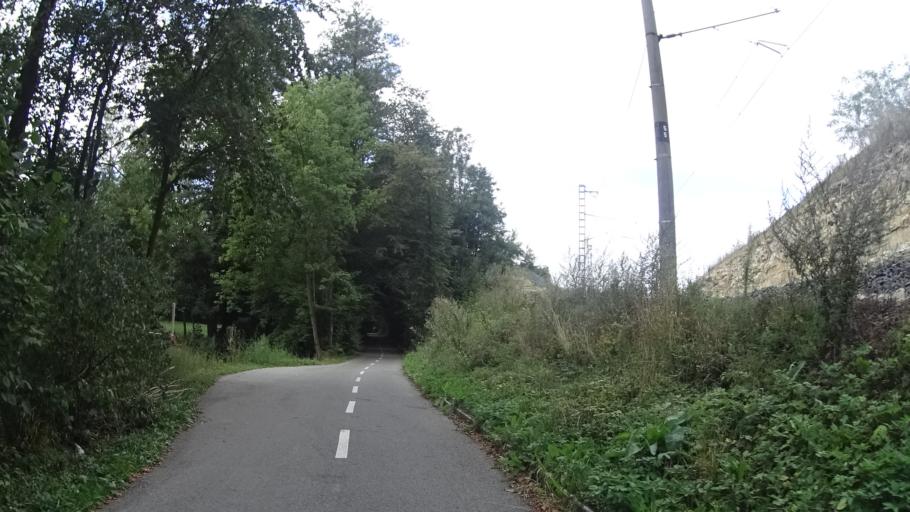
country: CZ
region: Pardubicky
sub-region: Okres Usti nad Orlici
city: Usti nad Orlici
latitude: 49.9858
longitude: 16.4059
